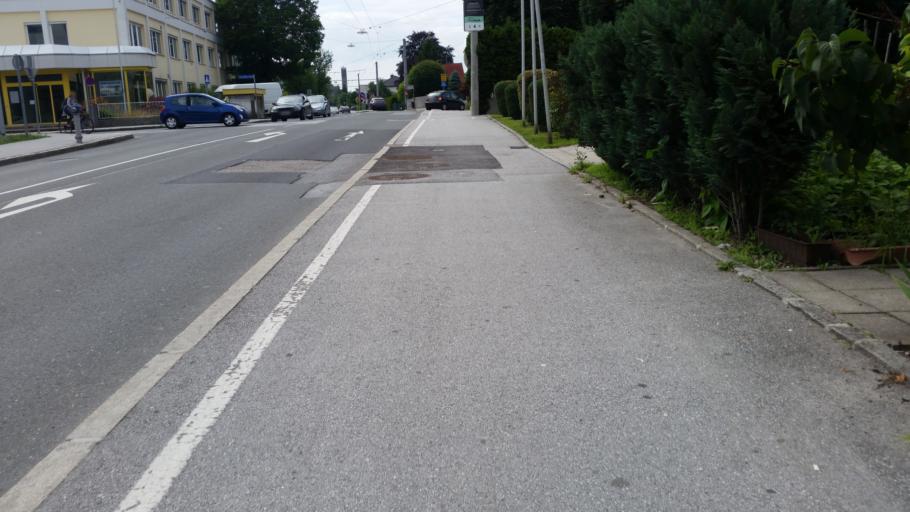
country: AT
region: Salzburg
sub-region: Salzburg Stadt
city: Salzburg
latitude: 47.8086
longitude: 13.0150
